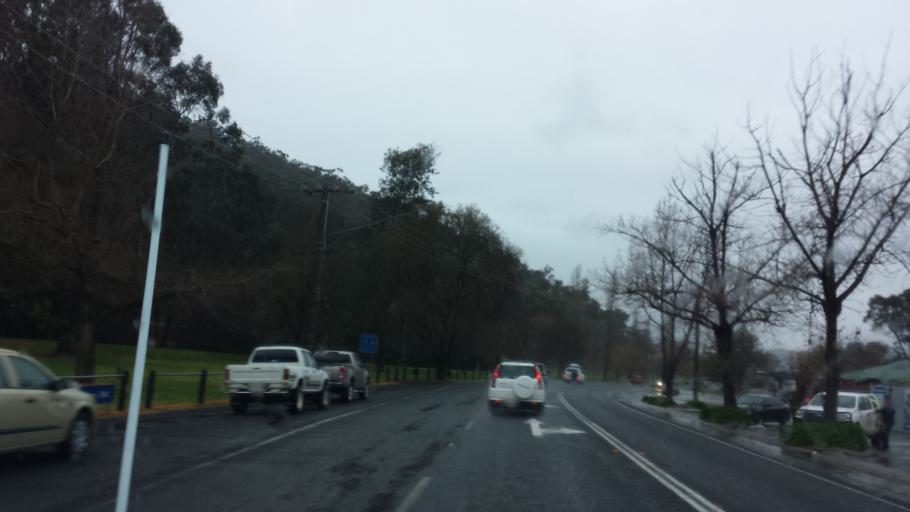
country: AU
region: Victoria
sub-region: Wangaratta
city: Wangaratta
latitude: -36.5654
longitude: 146.7292
